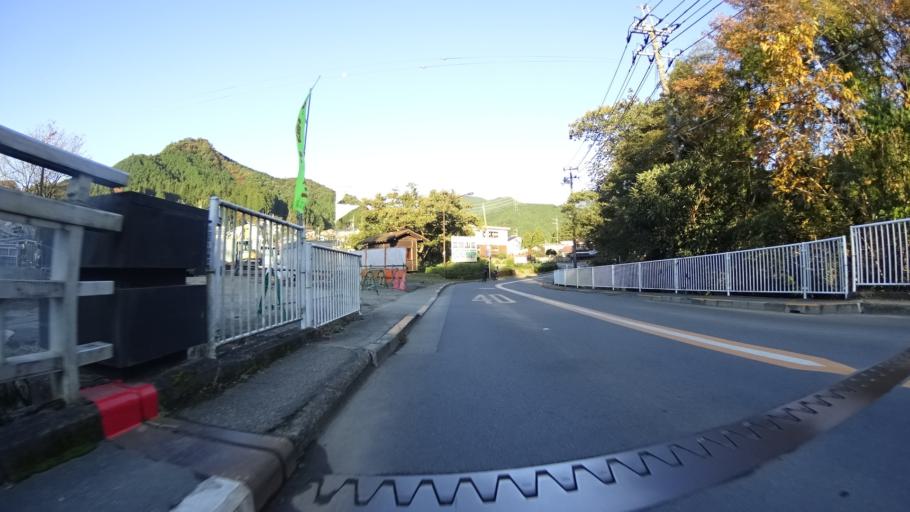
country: JP
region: Tokyo
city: Itsukaichi
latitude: 35.7270
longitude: 139.2070
